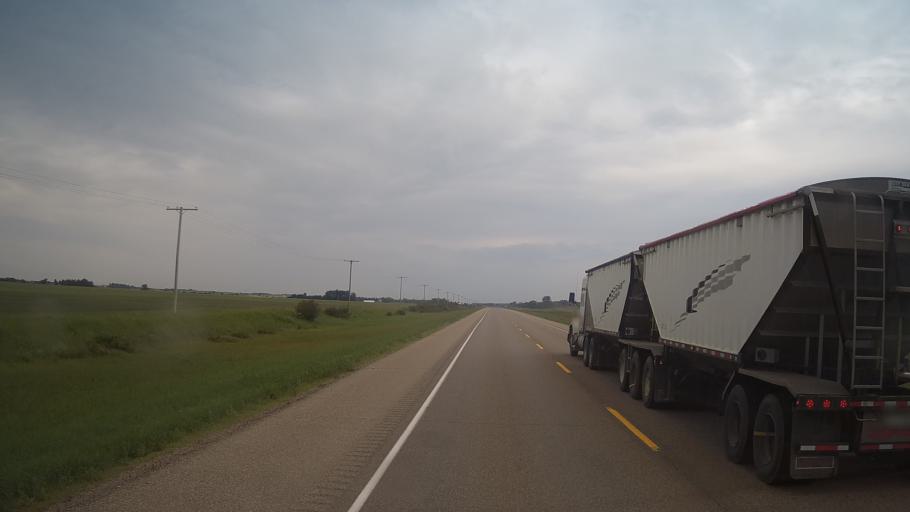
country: CA
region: Saskatchewan
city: Langham
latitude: 52.1289
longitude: -107.1967
